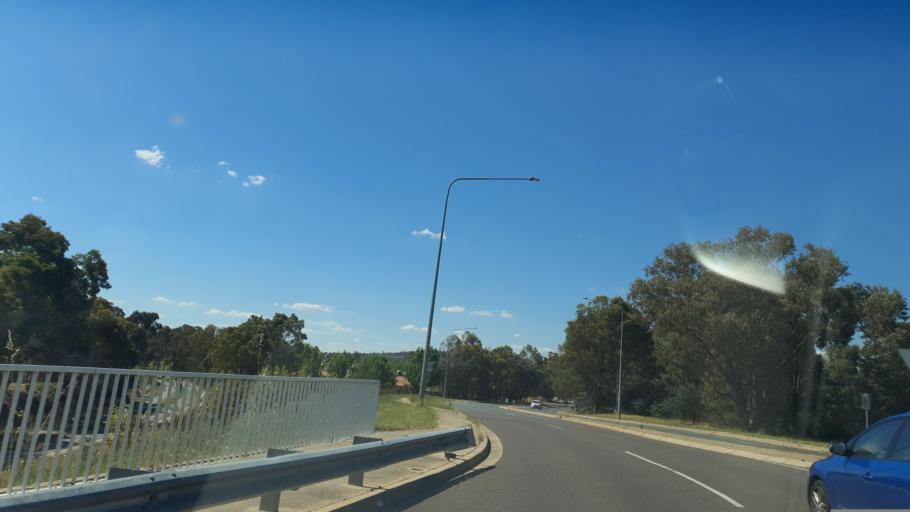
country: AU
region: Australian Capital Territory
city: Macquarie
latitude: -35.2322
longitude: 149.0618
